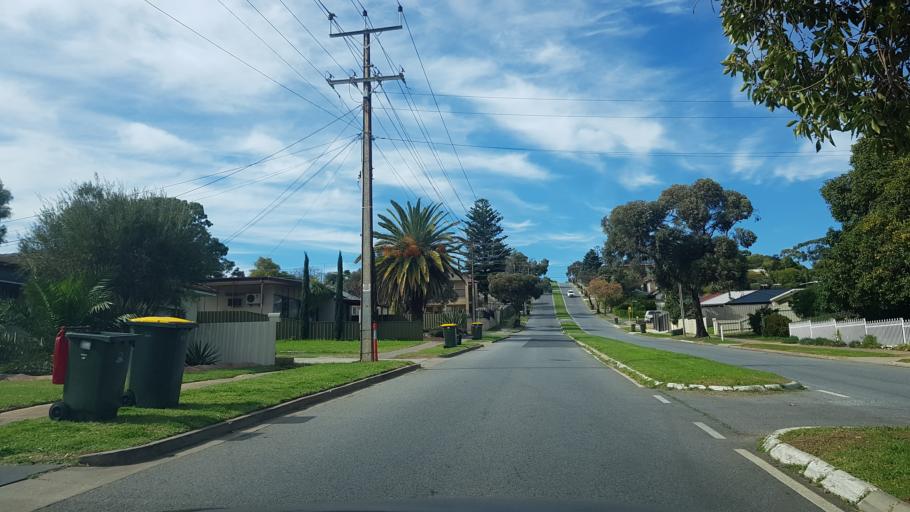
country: AU
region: South Australia
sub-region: Salisbury
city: Ingle Farm
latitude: -34.8103
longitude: 138.6551
